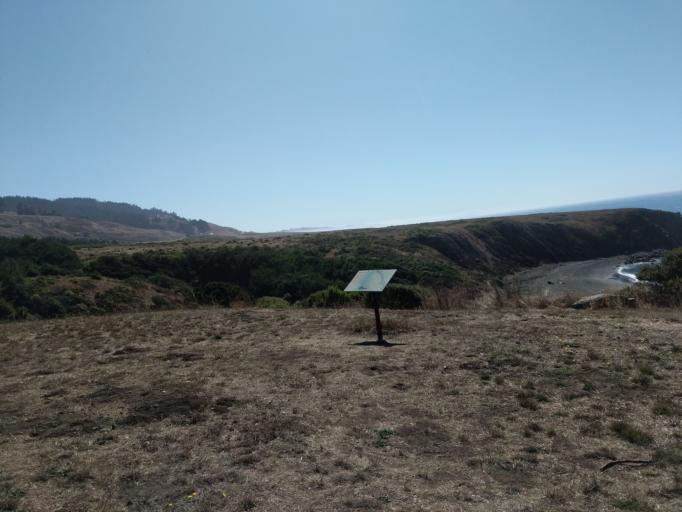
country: US
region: California
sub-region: Sonoma County
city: Monte Rio
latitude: 38.5136
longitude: -123.2435
